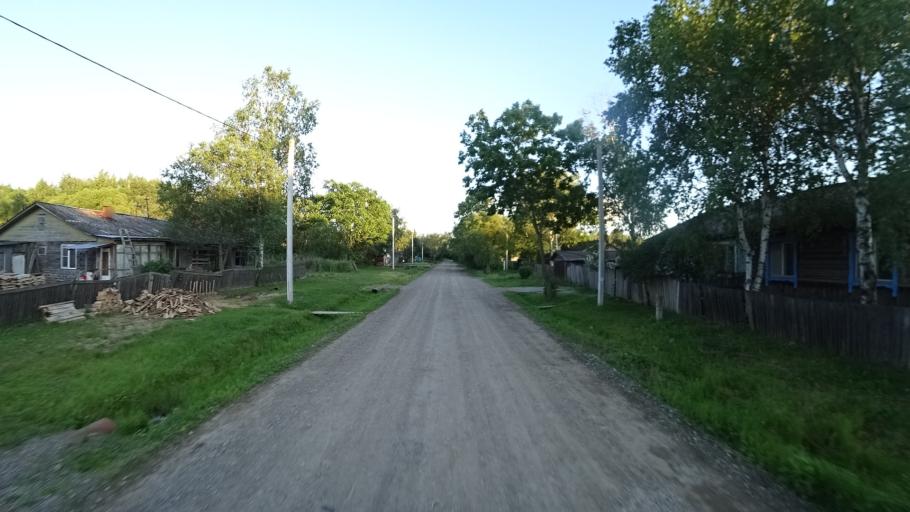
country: RU
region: Khabarovsk Krai
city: Khor
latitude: 47.8515
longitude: 134.9833
